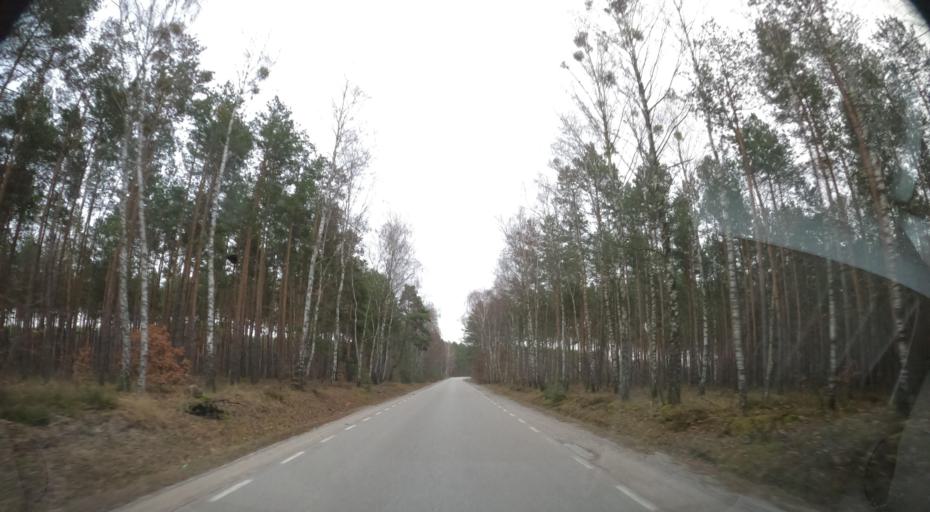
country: PL
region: Masovian Voivodeship
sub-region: Powiat radomski
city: Jedlinsk
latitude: 51.4916
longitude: 21.1594
